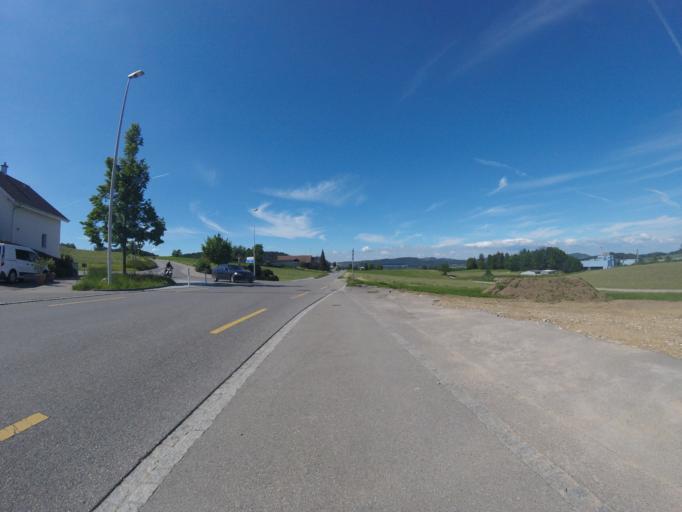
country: CH
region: Saint Gallen
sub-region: Wahlkreis Toggenburg
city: Kirchberg
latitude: 47.4200
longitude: 9.0624
